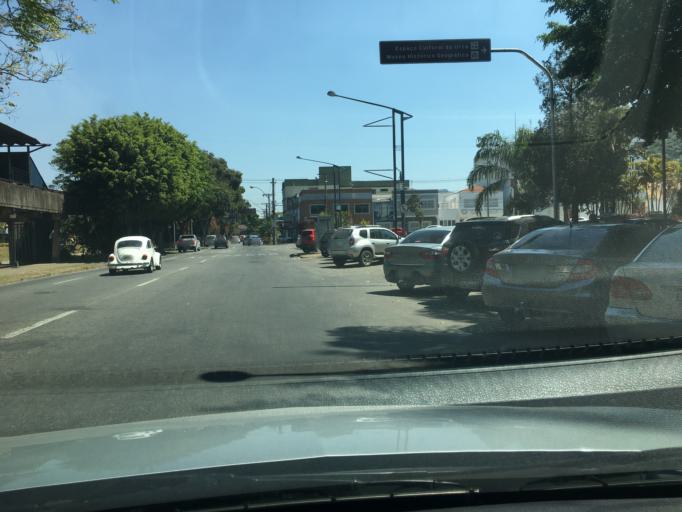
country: BR
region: Minas Gerais
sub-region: Pocos De Caldas
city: Pocos de Caldas
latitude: -21.7858
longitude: -46.5723
